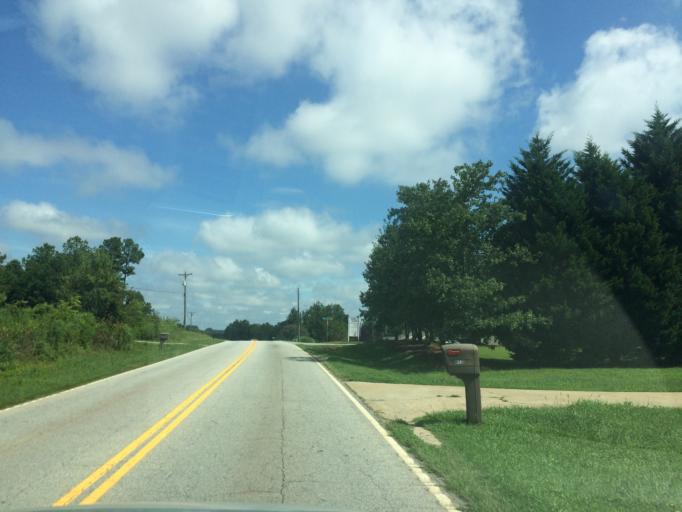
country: US
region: South Carolina
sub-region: Spartanburg County
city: Wellford
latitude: 34.9889
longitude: -82.1107
